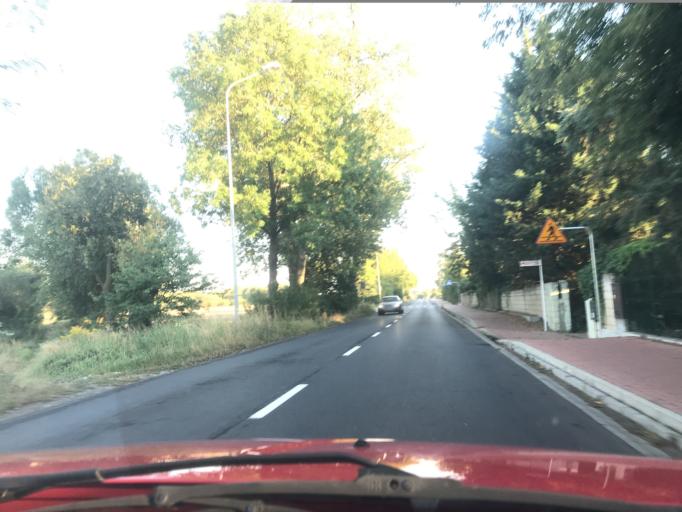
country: PL
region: Greater Poland Voivodeship
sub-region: Powiat poznanski
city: Baranowo
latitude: 52.4226
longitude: 16.7179
